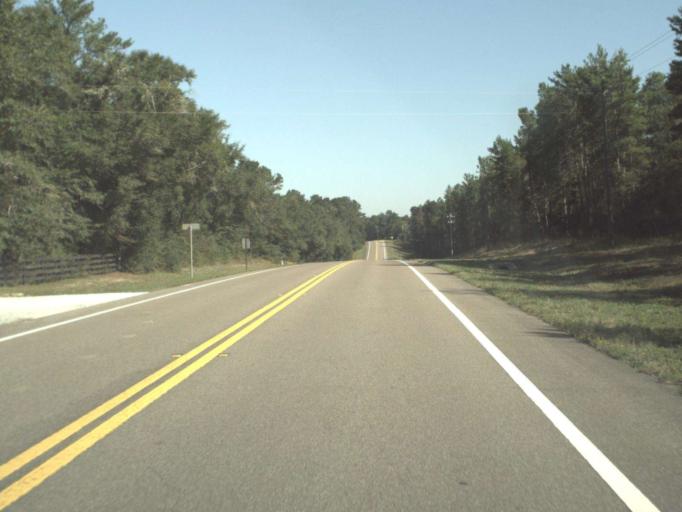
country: US
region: Florida
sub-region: Walton County
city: DeFuniak Springs
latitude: 30.5946
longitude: -85.9446
